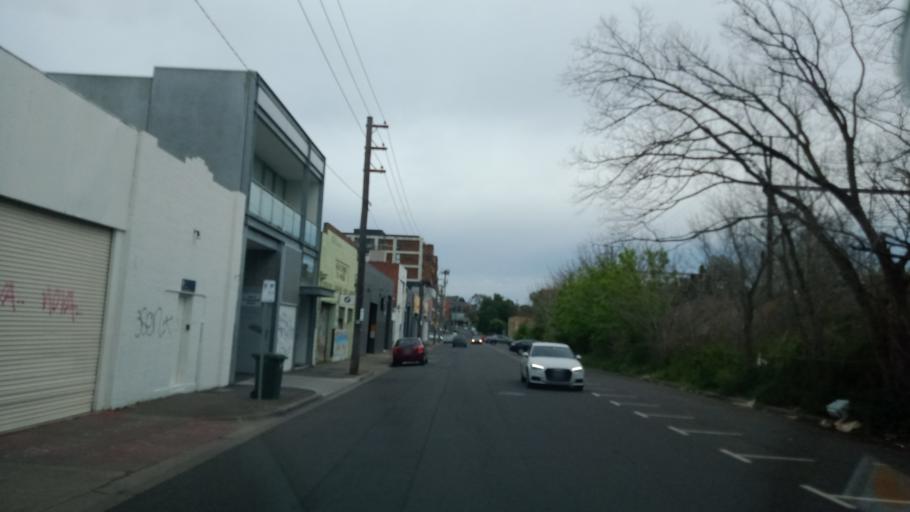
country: AU
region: Victoria
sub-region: Boroondara
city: Kew
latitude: -37.8214
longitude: 145.0311
